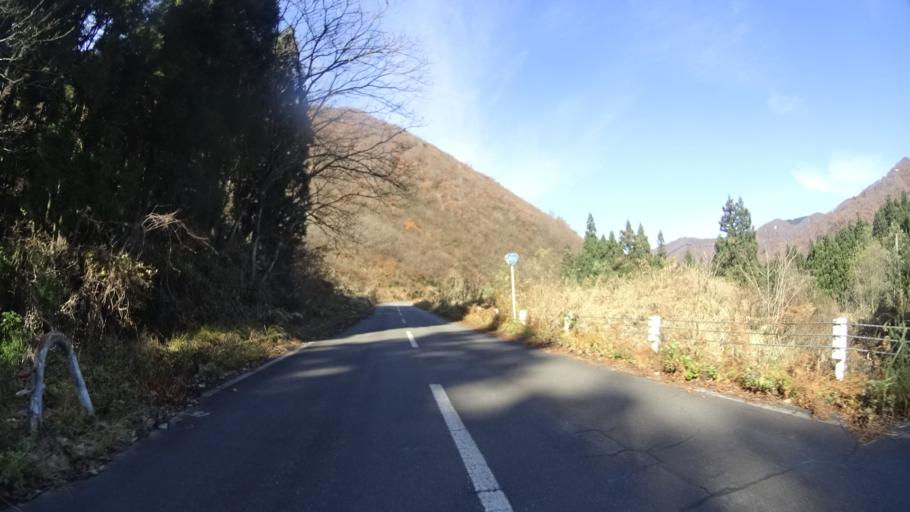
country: JP
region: Niigata
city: Muikamachi
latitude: 37.1823
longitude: 139.0807
